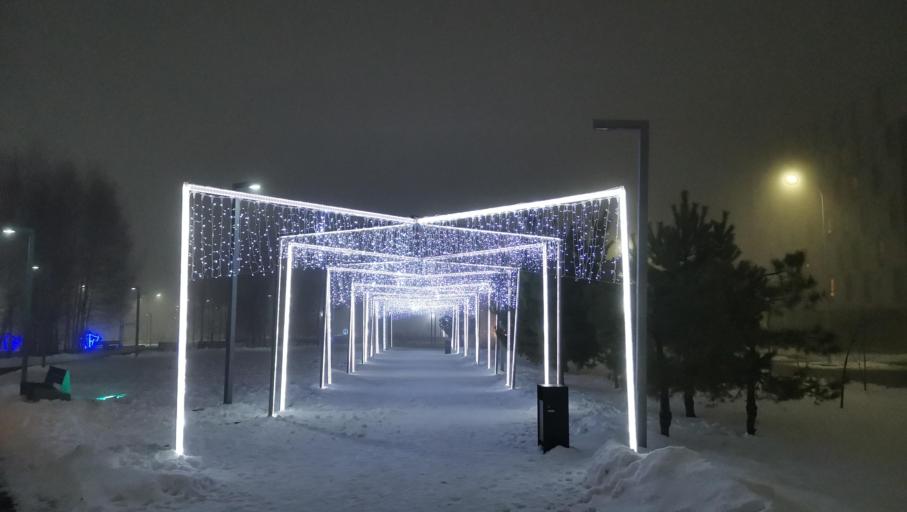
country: RU
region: Tatarstan
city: Sviyazhsk
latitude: 55.7464
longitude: 48.7435
